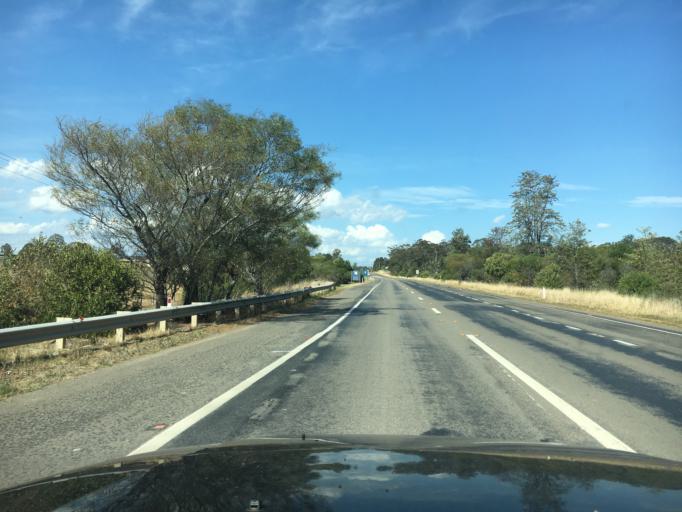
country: AU
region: New South Wales
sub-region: Cessnock
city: Branxton
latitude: -32.6556
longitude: 151.3400
